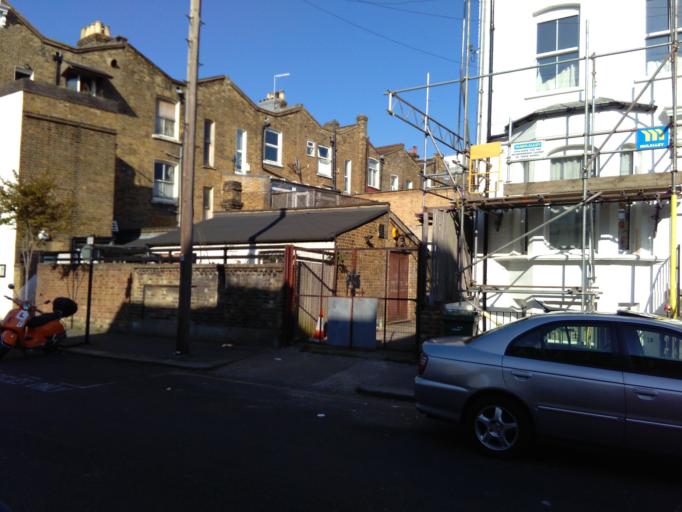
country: GB
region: England
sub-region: Greater London
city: Brixton Hill
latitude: 51.4592
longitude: -0.1248
